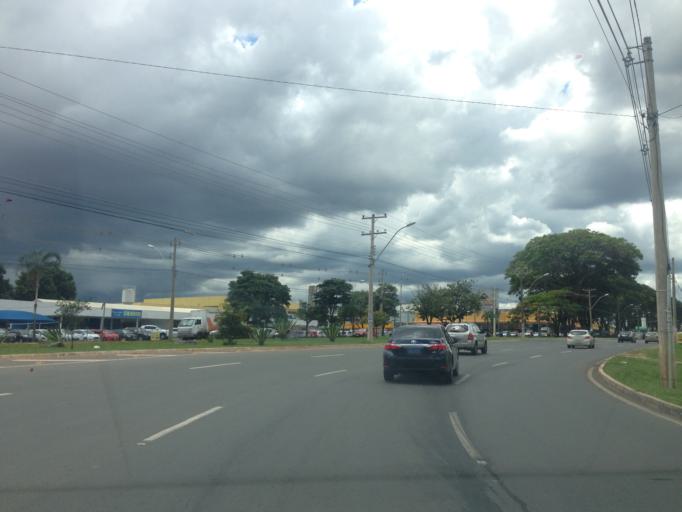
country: BR
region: Federal District
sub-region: Brasilia
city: Brasilia
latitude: -15.8072
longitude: -47.9512
